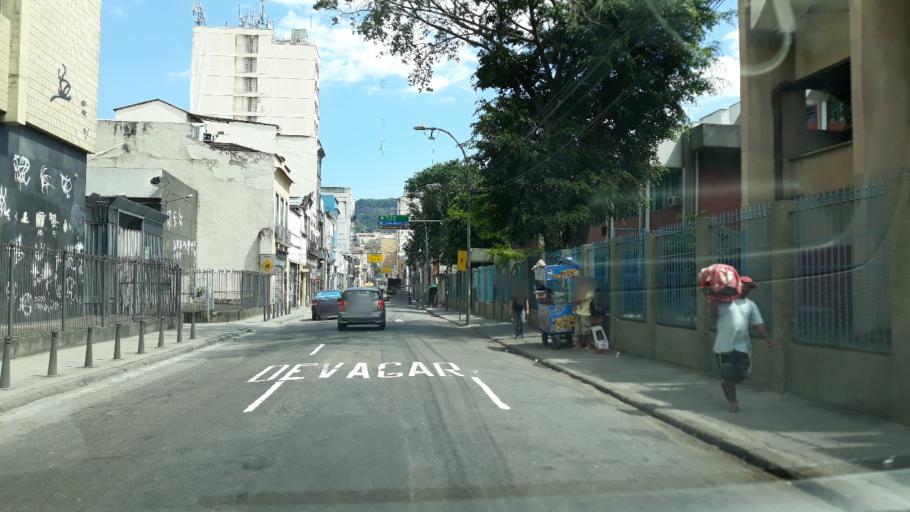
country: BR
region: Rio de Janeiro
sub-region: Rio De Janeiro
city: Rio de Janeiro
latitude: -22.9070
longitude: -43.1925
